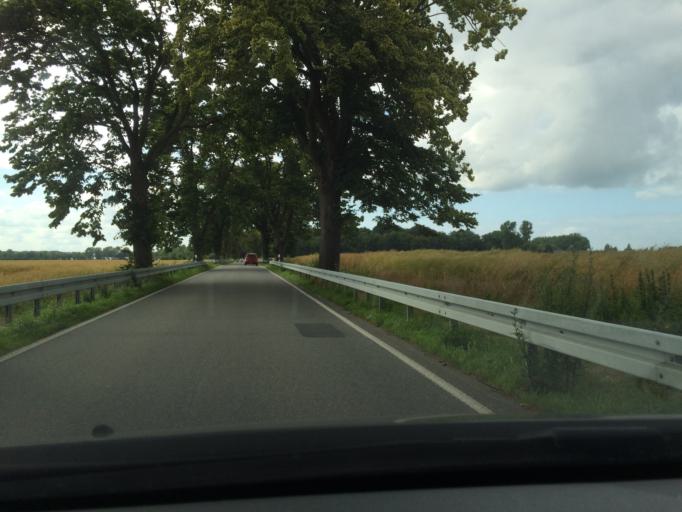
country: DE
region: Mecklenburg-Vorpommern
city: Preetz
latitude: 54.3934
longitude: 12.9848
